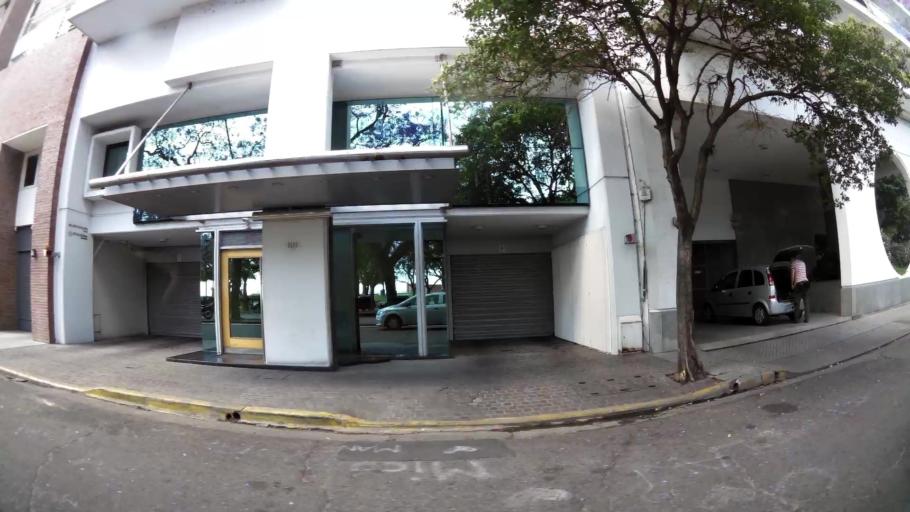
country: AR
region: Santa Fe
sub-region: Departamento de Rosario
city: Rosario
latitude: -32.9392
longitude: -60.6374
